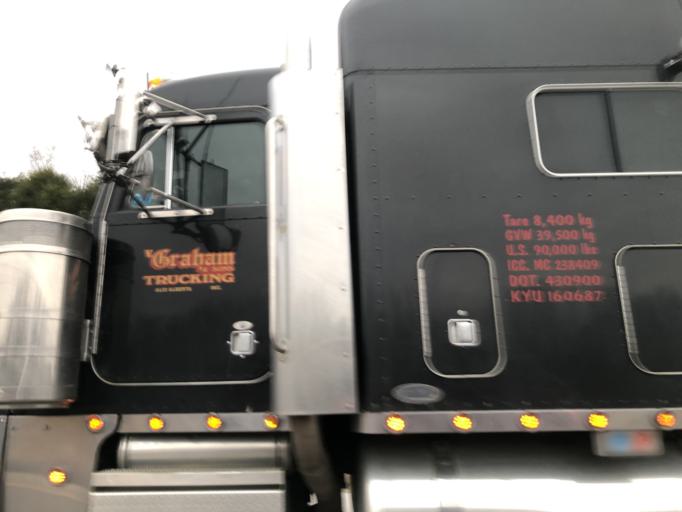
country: US
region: Illinois
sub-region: Johnson County
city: Vienna
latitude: 37.3328
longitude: -88.7773
